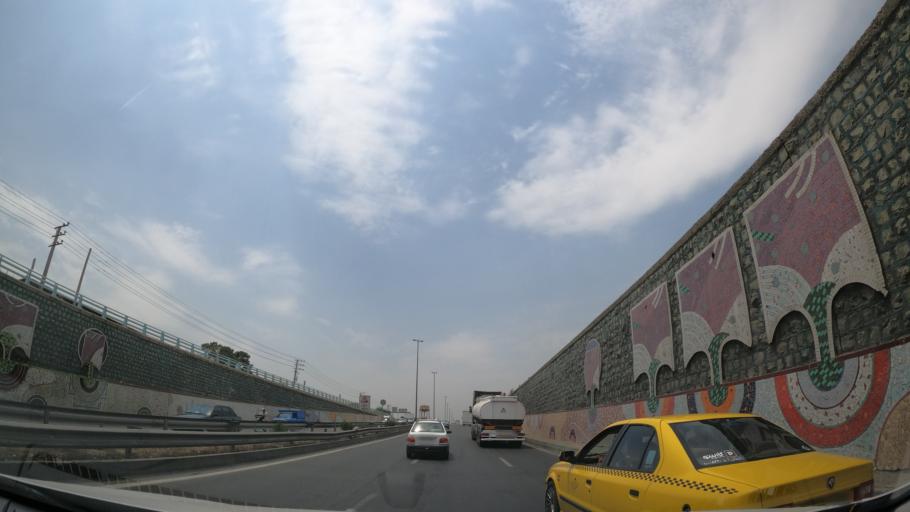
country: IR
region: Tehran
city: Shahr-e Qods
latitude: 35.6923
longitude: 51.2114
